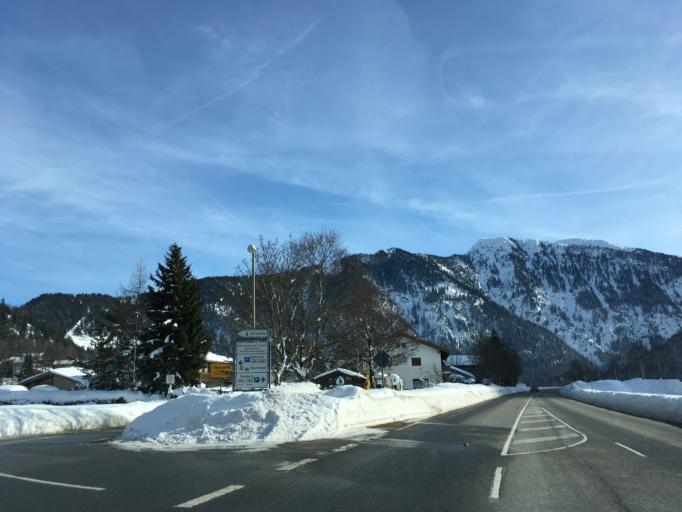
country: DE
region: Bavaria
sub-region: Upper Bavaria
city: Bayrischzell
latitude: 47.6785
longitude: 12.0032
